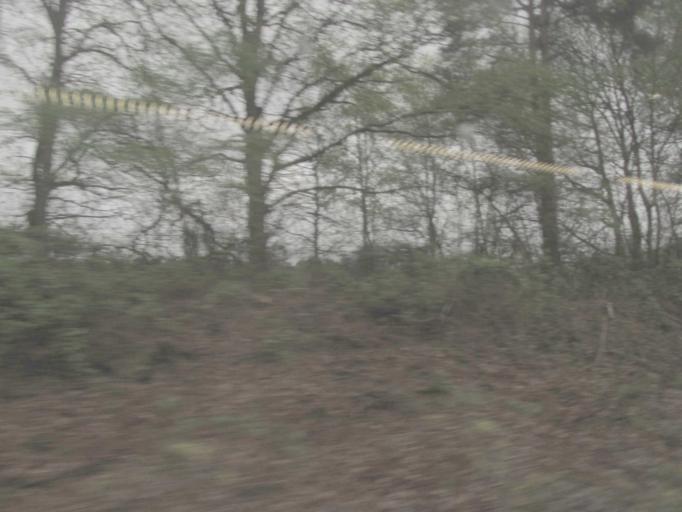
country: GB
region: England
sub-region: Hampshire
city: Yateley
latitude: 51.3583
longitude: -0.8143
